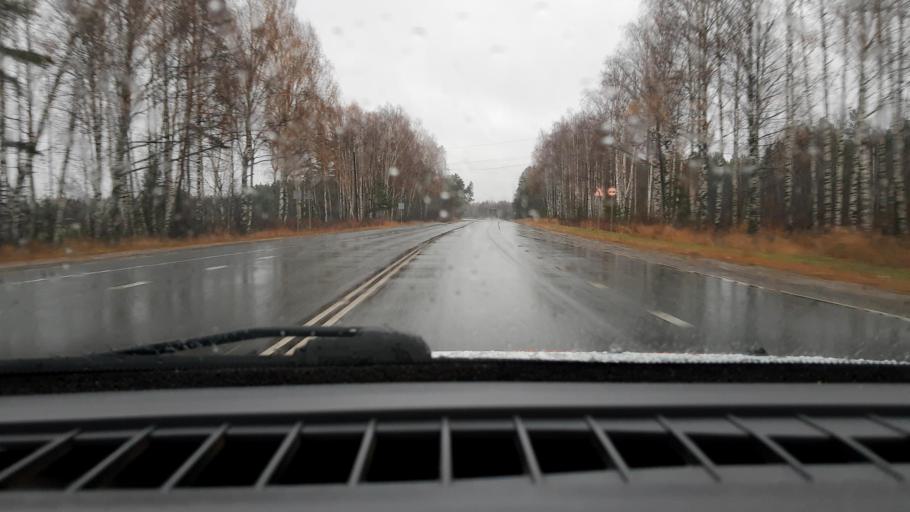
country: RU
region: Nizjnij Novgorod
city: Linda
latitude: 56.6576
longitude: 44.1234
